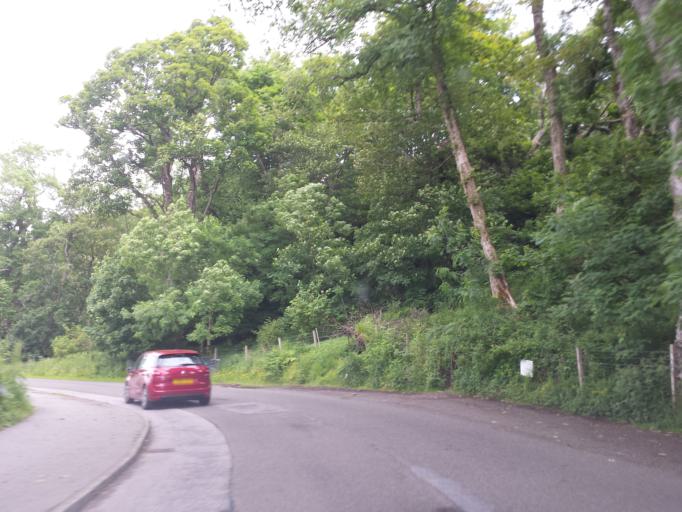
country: GB
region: Scotland
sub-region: Argyll and Bute
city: Oban
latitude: 56.4269
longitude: -5.4853
